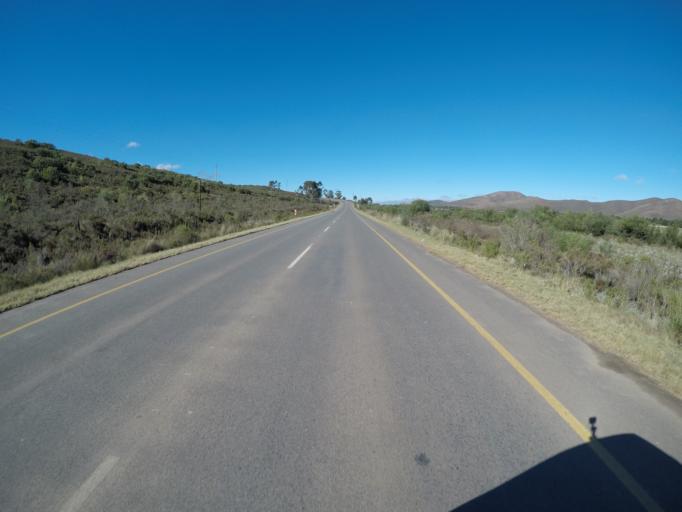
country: ZA
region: Western Cape
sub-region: Overberg District Municipality
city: Caledon
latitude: -34.0542
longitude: 19.5942
